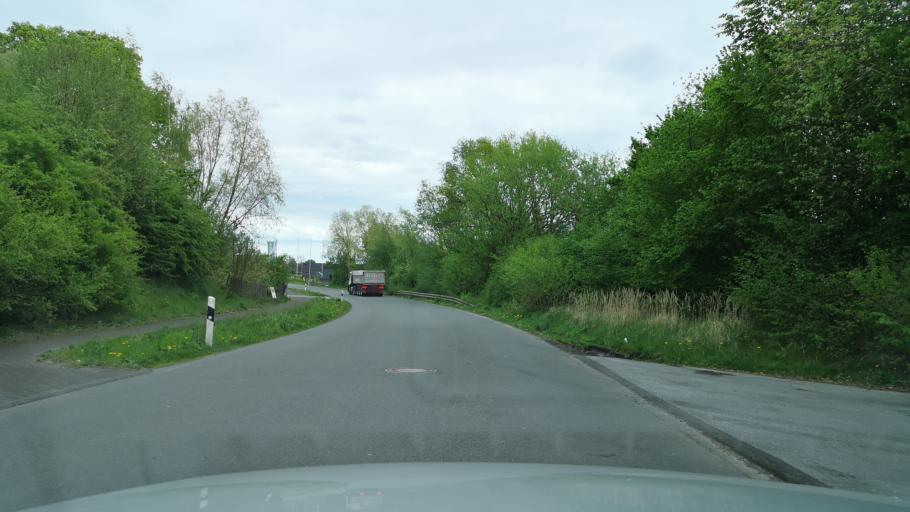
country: DE
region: North Rhine-Westphalia
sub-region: Regierungsbezirk Arnsberg
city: Menden
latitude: 51.4486
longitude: 7.7507
